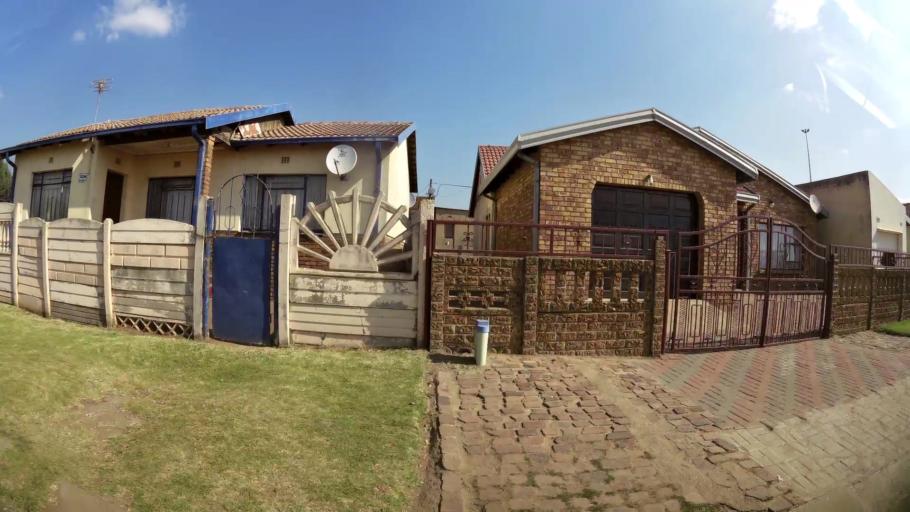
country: ZA
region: Gauteng
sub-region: Ekurhuleni Metropolitan Municipality
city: Benoni
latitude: -26.1406
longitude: 28.4138
